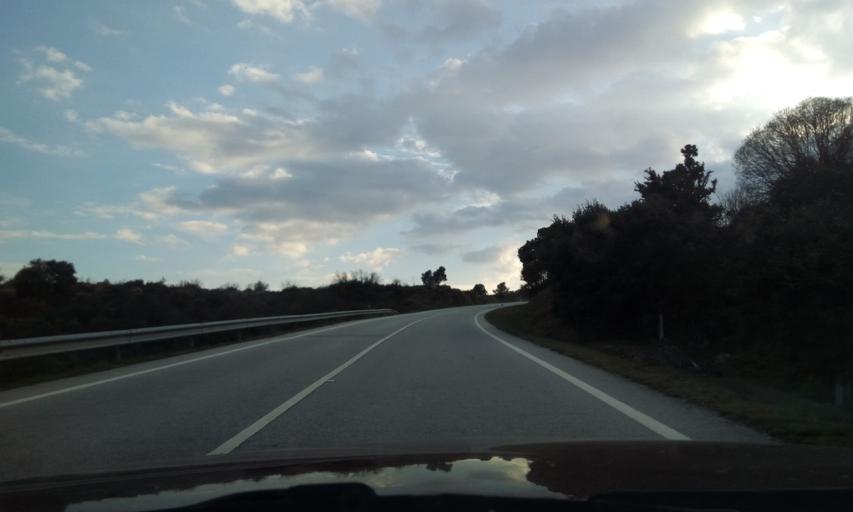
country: ES
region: Castille and Leon
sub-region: Provincia de Salamanca
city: Aldea del Obispo
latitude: 40.6899
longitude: -6.9412
